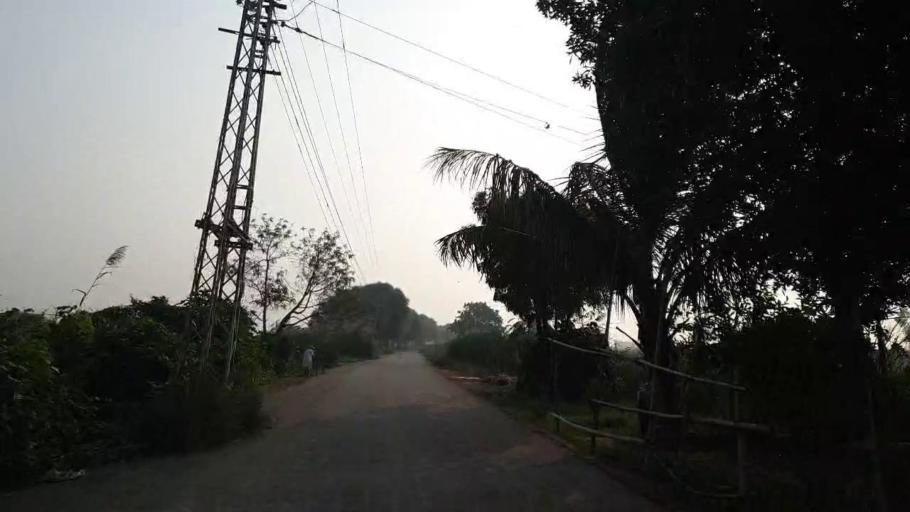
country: PK
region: Sindh
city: Tando Muhammad Khan
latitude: 25.1266
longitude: 68.5546
